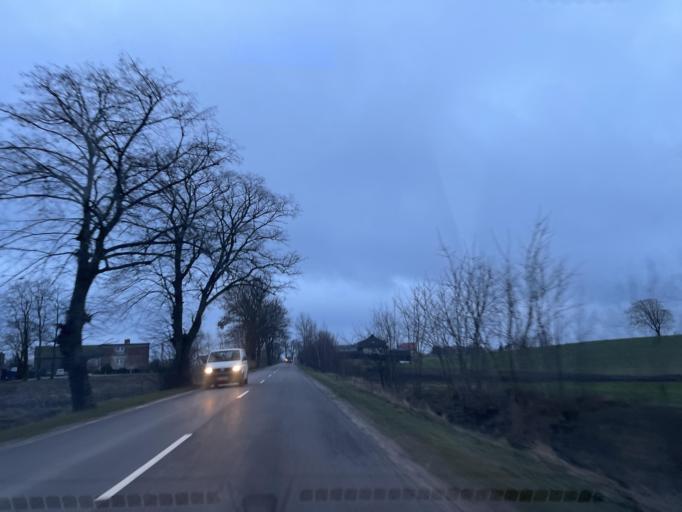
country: PL
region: Pomeranian Voivodeship
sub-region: Powiat kartuski
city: Kartuzy
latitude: 54.4111
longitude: 18.2071
